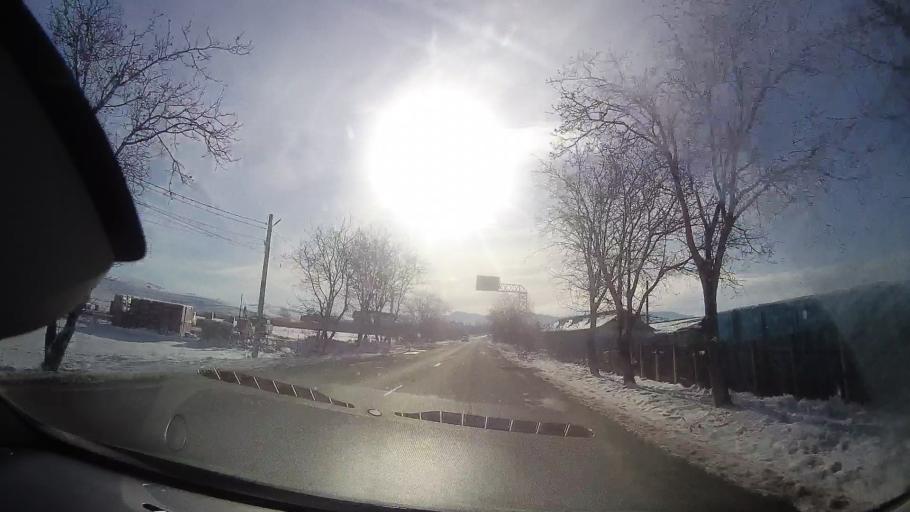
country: RO
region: Neamt
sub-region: Comuna Baltatesti
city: Valea Seaca
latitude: 47.1423
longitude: 26.3186
